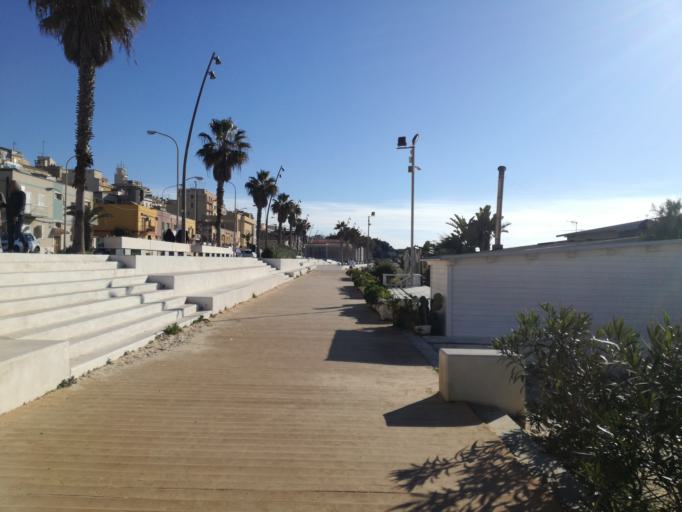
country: IT
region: Sicily
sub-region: Provincia di Caltanissetta
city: Gela
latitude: 37.0652
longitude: 14.2448
